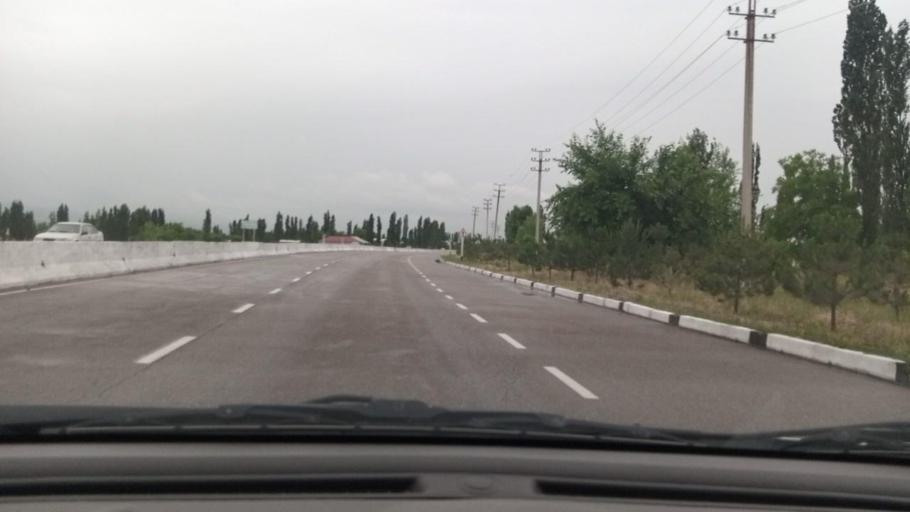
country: UZ
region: Toshkent
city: Ohangaron
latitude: 40.9162
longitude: 69.8298
